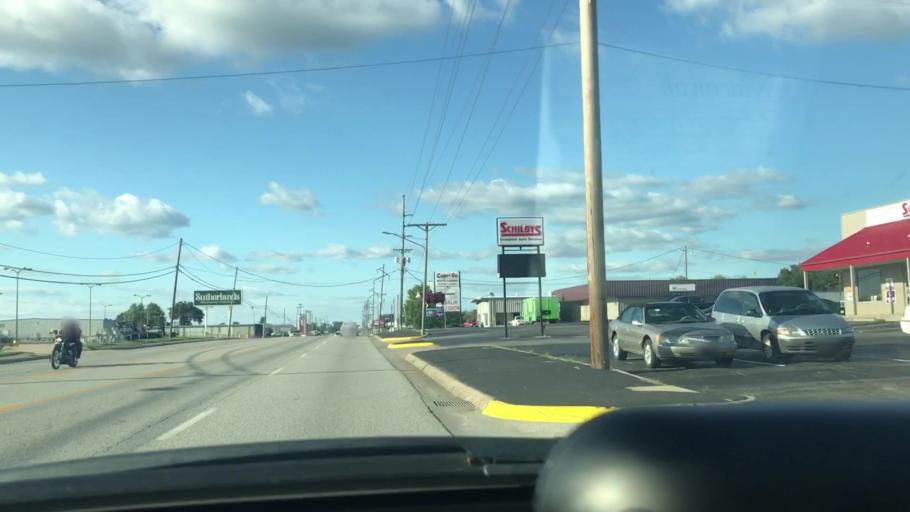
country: US
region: Missouri
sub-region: Pettis County
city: Sedalia
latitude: 38.6765
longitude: -93.2515
